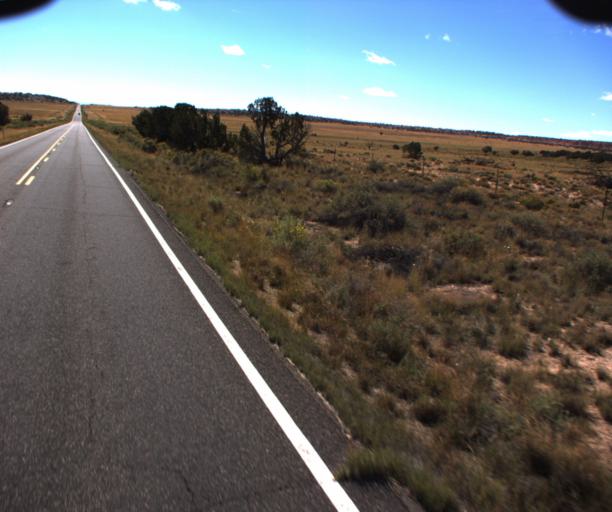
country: US
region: Arizona
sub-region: Apache County
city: Saint Johns
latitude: 34.7727
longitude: -109.2401
